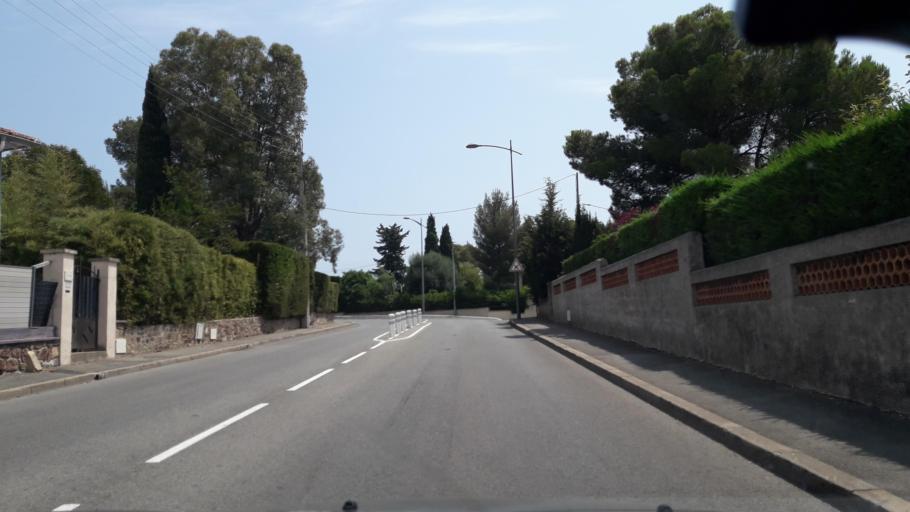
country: FR
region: Provence-Alpes-Cote d'Azur
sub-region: Departement du Var
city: Saint-Raphael
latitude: 43.4208
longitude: 6.7841
